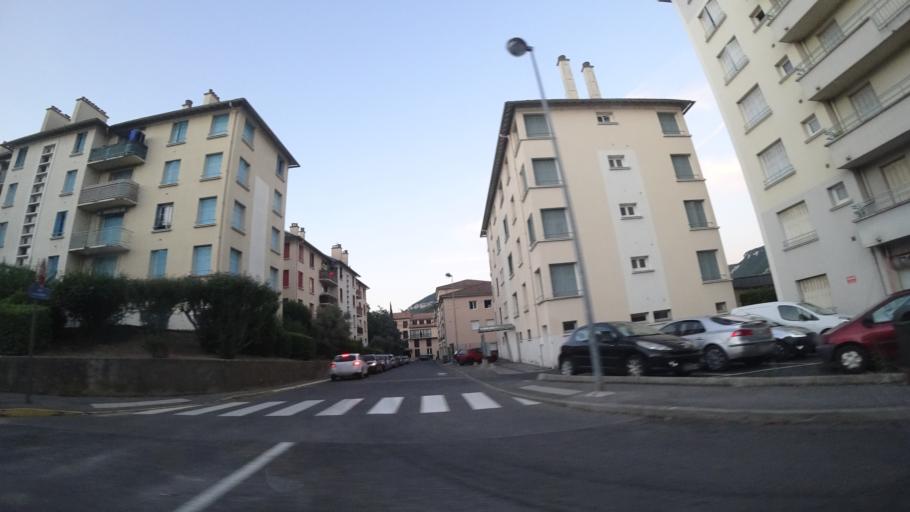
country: FR
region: Midi-Pyrenees
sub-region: Departement de l'Aveyron
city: Millau
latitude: 44.0949
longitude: 3.0734
